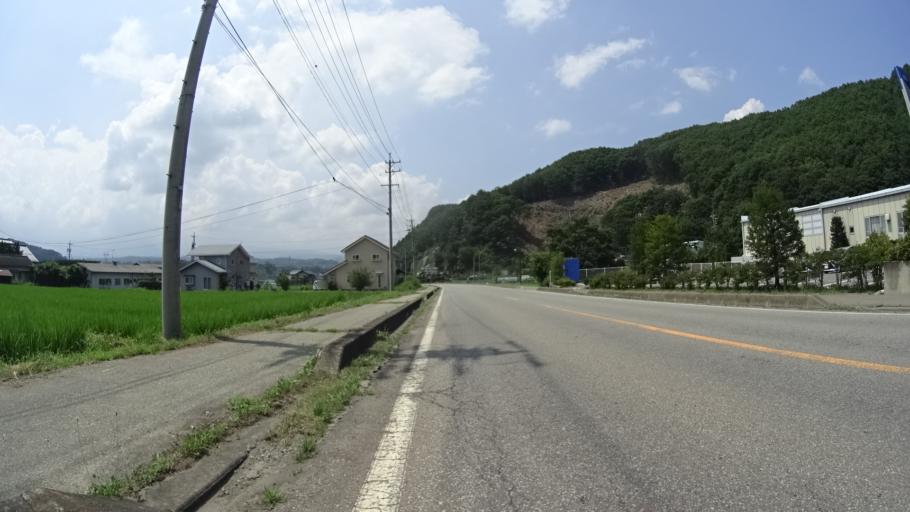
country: JP
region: Nagano
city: Saku
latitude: 36.1549
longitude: 138.4999
